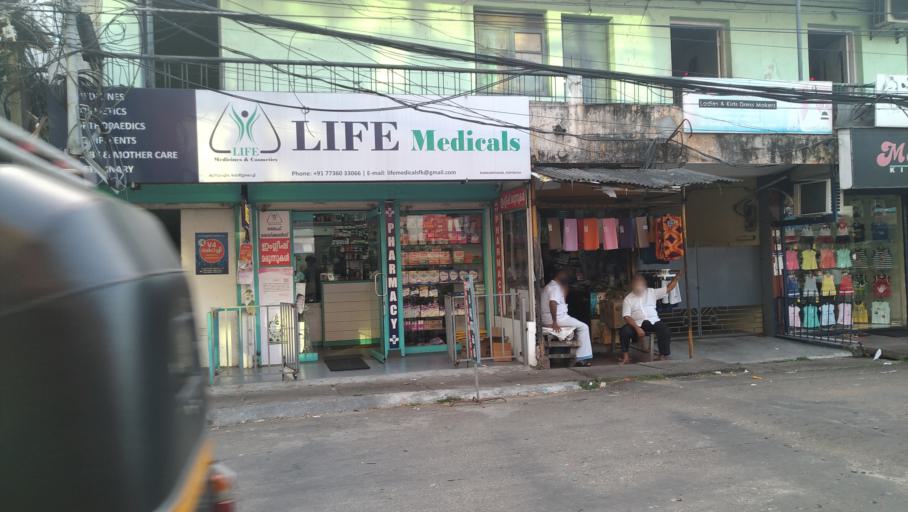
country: IN
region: Kerala
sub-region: Ernakulam
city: Cochin
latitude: 9.9639
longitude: 76.2456
